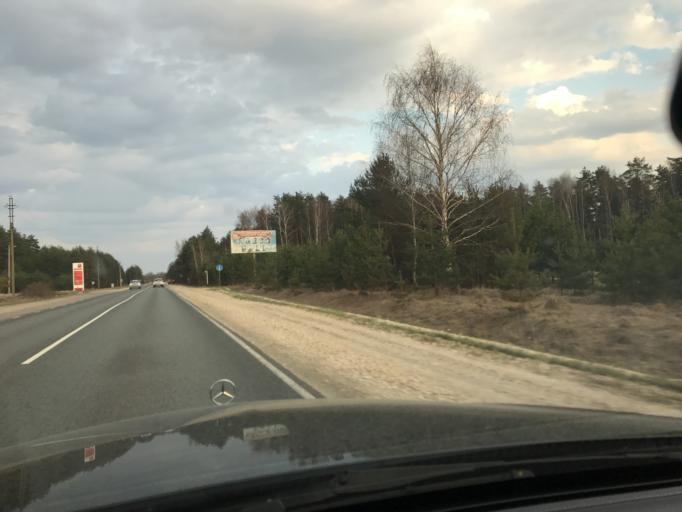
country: RU
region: Vladimir
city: Murom
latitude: 55.6219
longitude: 41.9076
